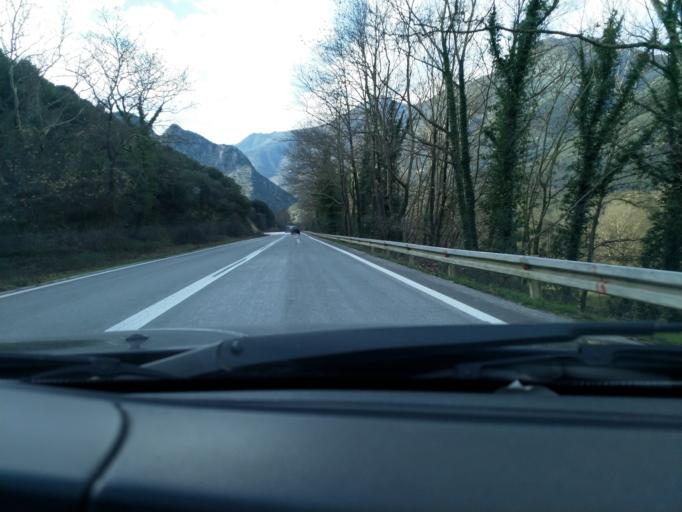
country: GR
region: Epirus
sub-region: Nomos Prevezis
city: Pappadates
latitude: 39.4110
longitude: 20.8423
